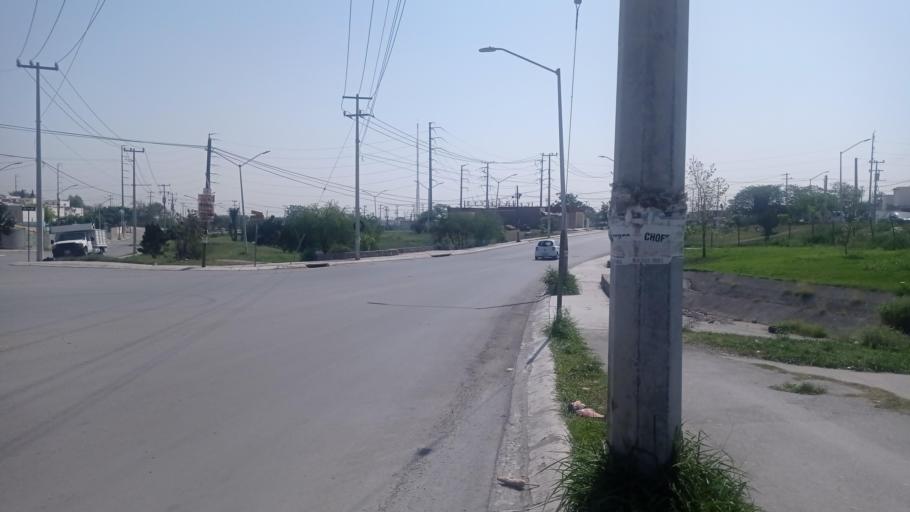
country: MX
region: Nuevo Leon
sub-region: Juarez
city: Monte Kristal
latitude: 25.6105
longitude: -100.1592
